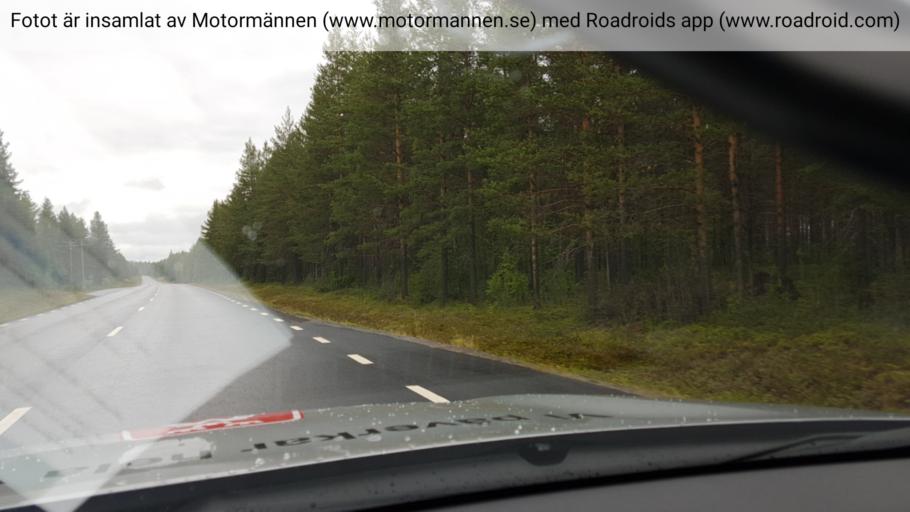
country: SE
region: Norrbotten
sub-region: Alvsbyns Kommun
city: AElvsbyn
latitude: 66.2510
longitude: 20.8533
